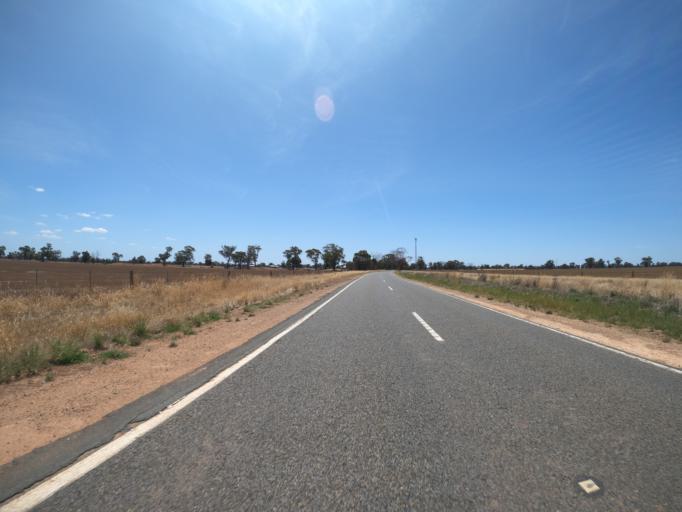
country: AU
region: Victoria
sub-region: Moira
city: Yarrawonga
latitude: -36.1920
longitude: 145.9670
